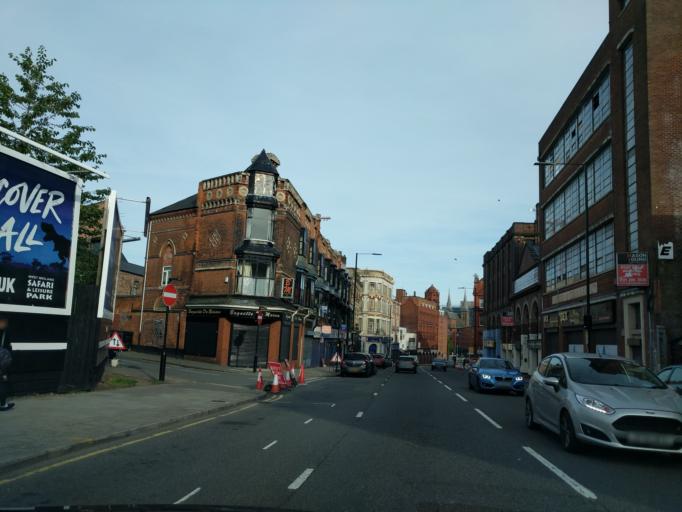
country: GB
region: England
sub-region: City and Borough of Birmingham
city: Birmingham
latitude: 52.4874
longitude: -1.9036
